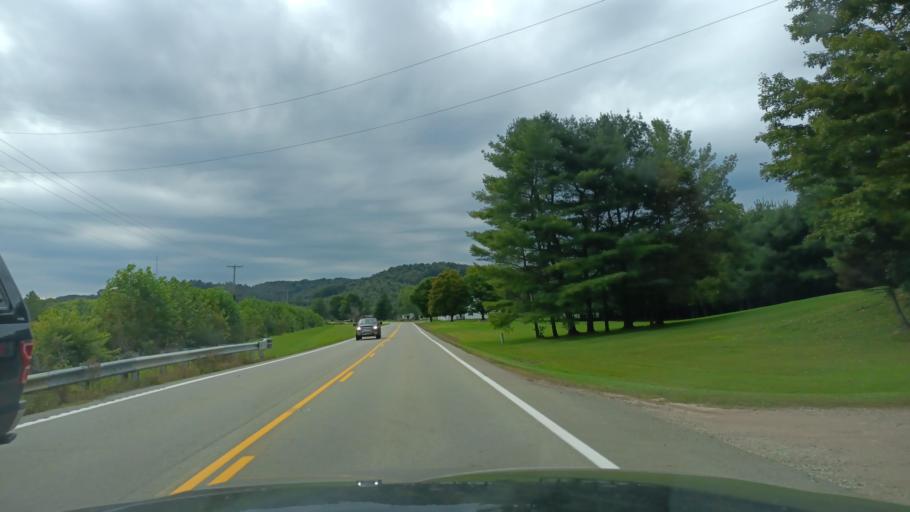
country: US
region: Ohio
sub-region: Vinton County
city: McArthur
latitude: 39.2707
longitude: -82.6685
